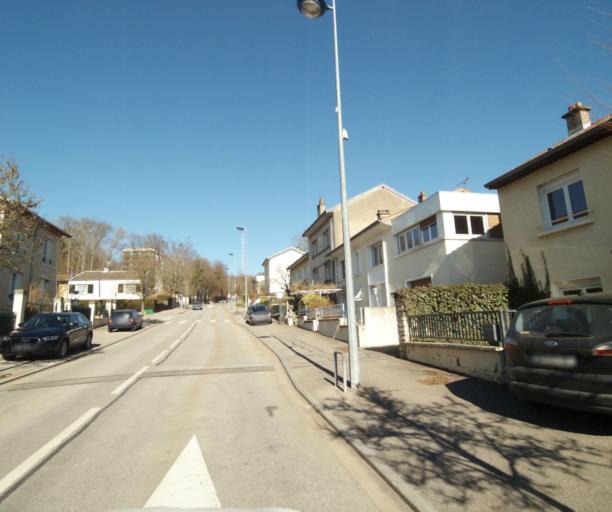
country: FR
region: Lorraine
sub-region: Departement de Meurthe-et-Moselle
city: Saint-Max
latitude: 48.7081
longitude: 6.2041
